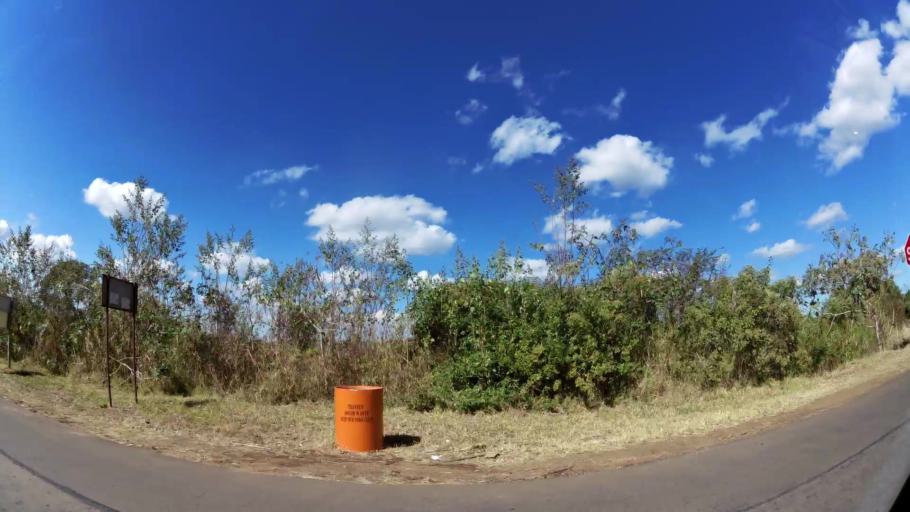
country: ZA
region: Limpopo
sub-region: Mopani District Municipality
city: Tzaneen
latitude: -23.8412
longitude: 30.1503
